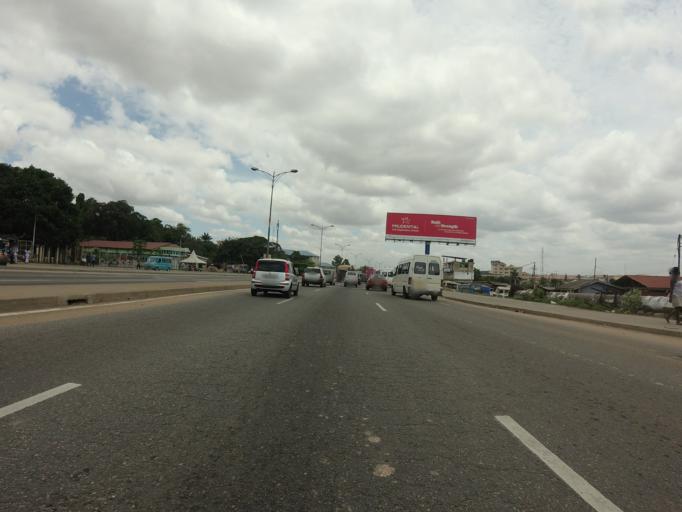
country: GH
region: Greater Accra
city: Gbawe
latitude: 5.5670
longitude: -0.2880
